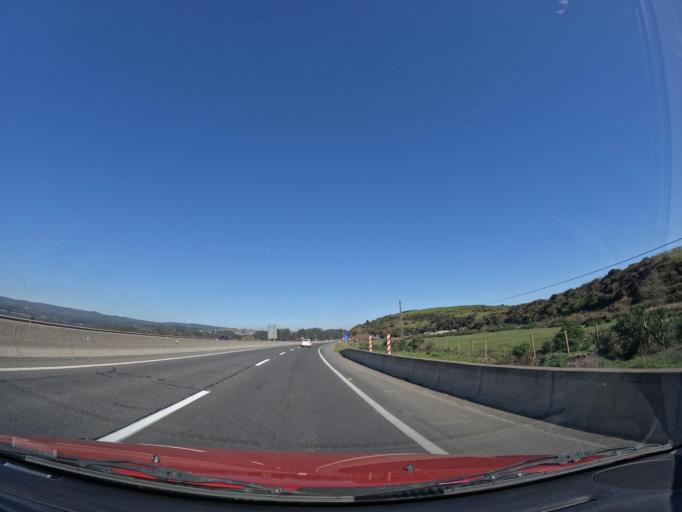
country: CL
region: Biobio
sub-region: Provincia de Concepcion
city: Coronel
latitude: -37.0116
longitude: -73.1307
